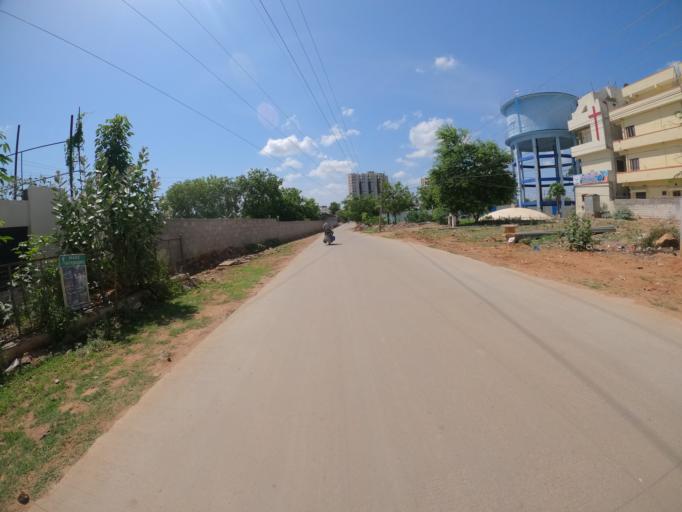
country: IN
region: Telangana
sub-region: Hyderabad
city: Hyderabad
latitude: 17.3584
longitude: 78.3817
